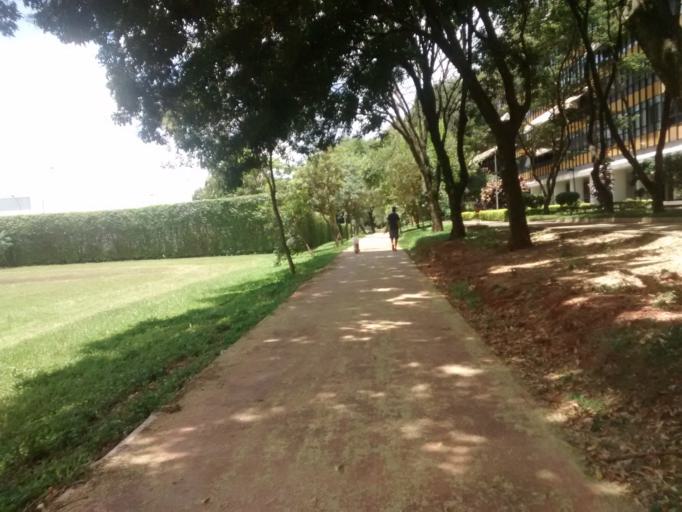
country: BR
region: Federal District
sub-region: Brasilia
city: Brasilia
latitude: -15.7663
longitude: -47.8884
